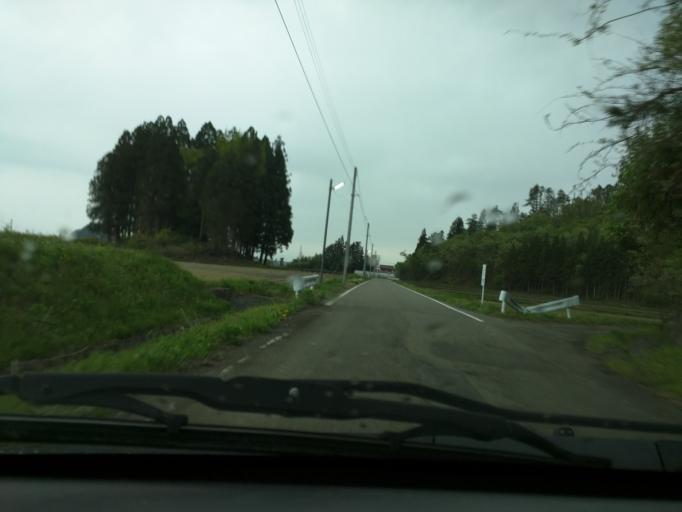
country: JP
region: Fukushima
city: Kitakata
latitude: 37.4304
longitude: 139.8877
